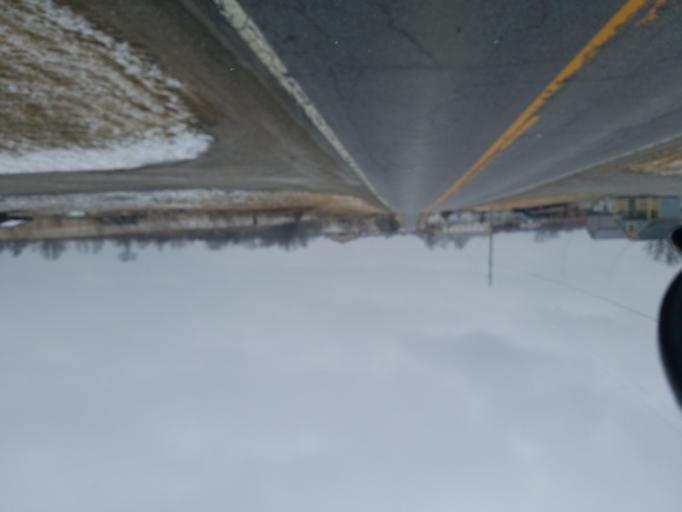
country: US
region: Missouri
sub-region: Putnam County
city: Unionville
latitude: 40.4958
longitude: -93.0093
